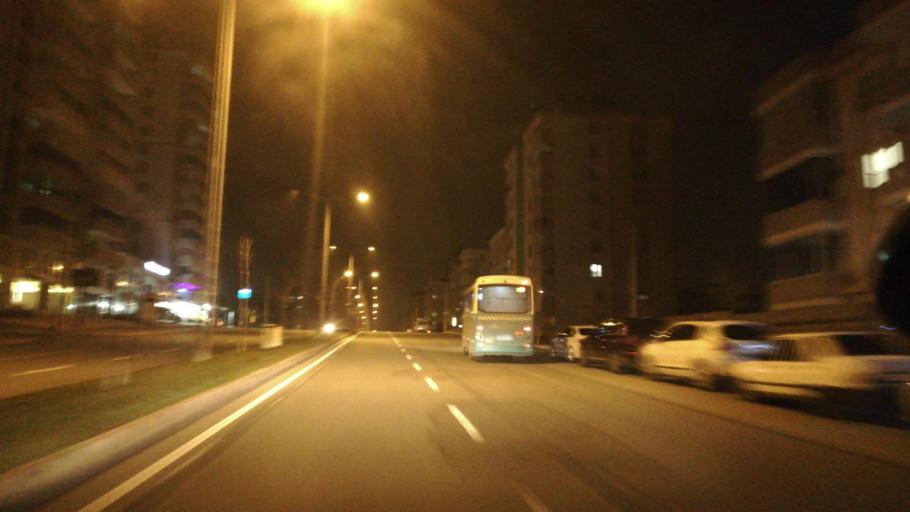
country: TR
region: Kahramanmaras
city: Kahramanmaras
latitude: 37.5966
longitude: 36.8778
